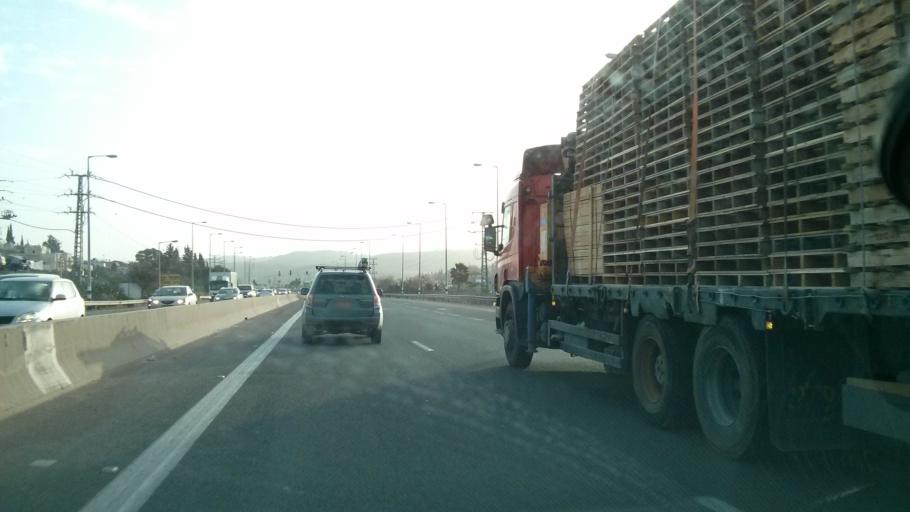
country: PS
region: West Bank
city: Barta`ah ash Sharqiyah
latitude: 32.5018
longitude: 35.0765
